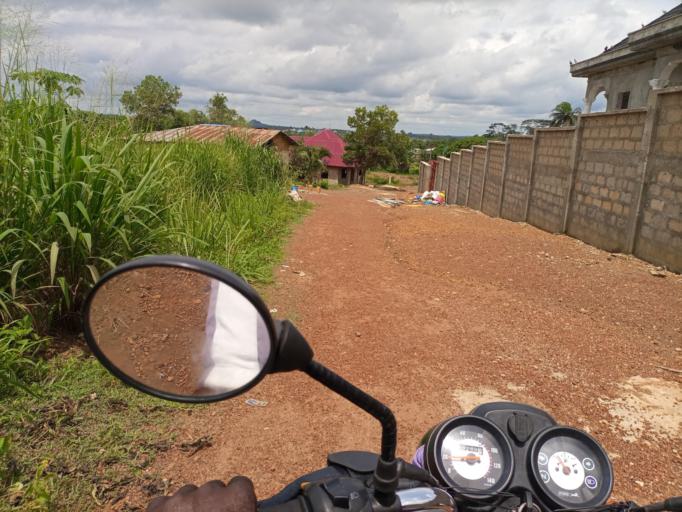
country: SL
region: Southern Province
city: Bo
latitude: 7.9745
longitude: -11.7650
